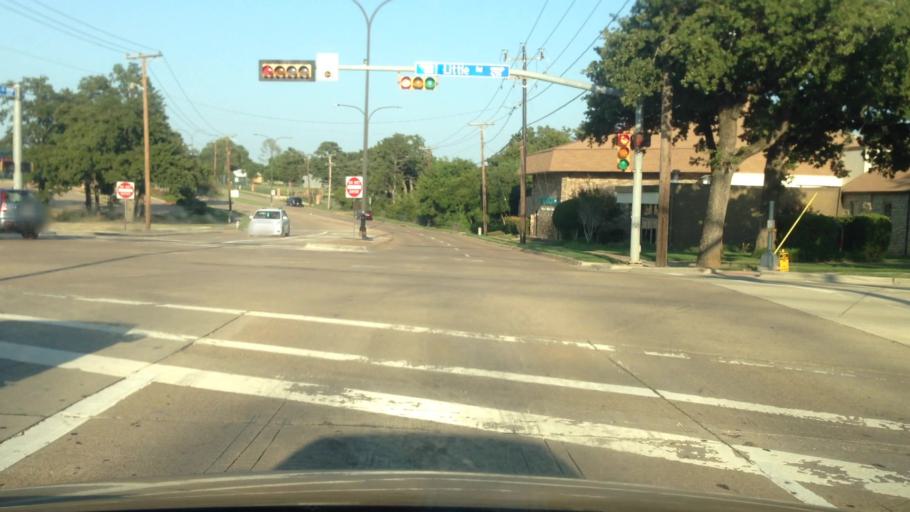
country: US
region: Texas
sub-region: Tarrant County
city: Dalworthington Gardens
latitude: 32.6816
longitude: -97.1936
